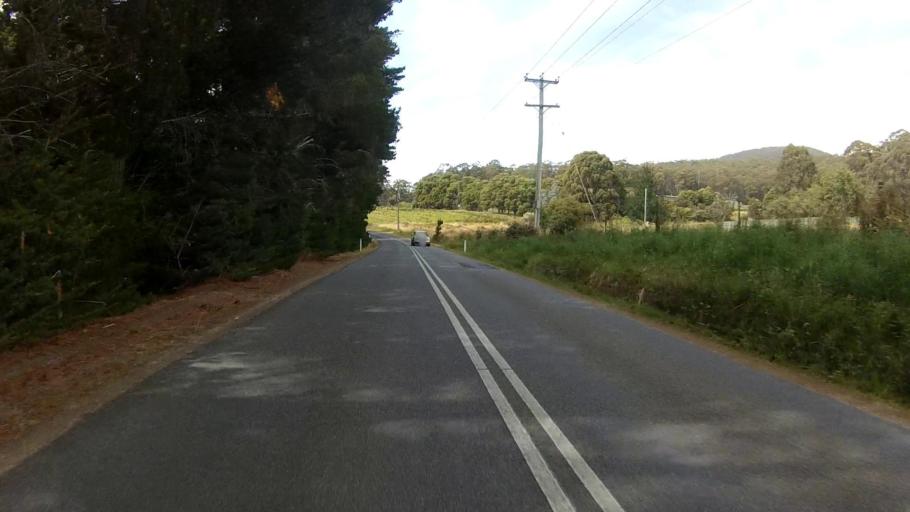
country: AU
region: Tasmania
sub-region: Kingborough
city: Kettering
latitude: -43.1864
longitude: 147.2426
